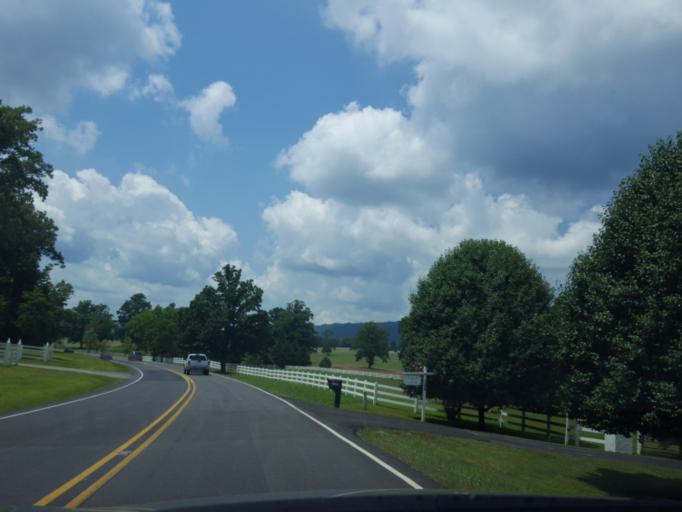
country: US
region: Virginia
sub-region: Orange County
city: Gordonsville
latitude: 38.1159
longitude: -78.2400
